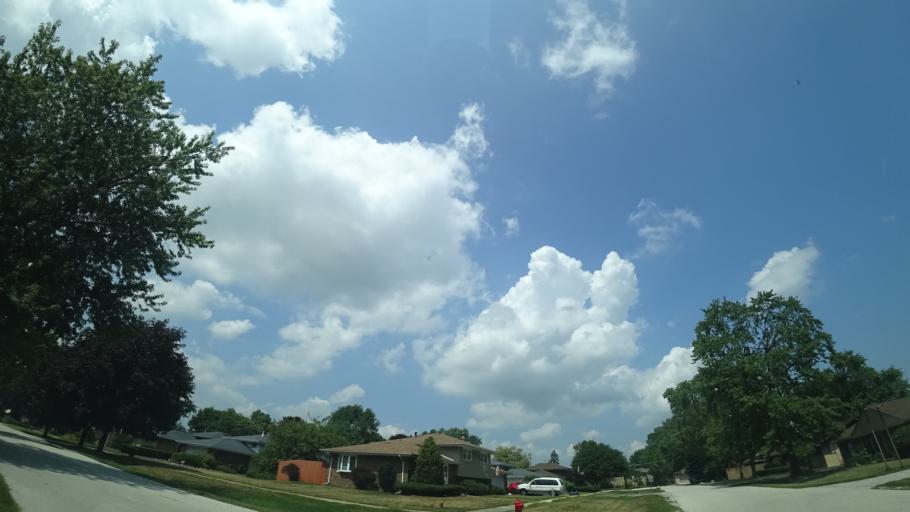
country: US
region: Illinois
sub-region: Cook County
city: Worth
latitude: 41.6964
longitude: -87.7915
